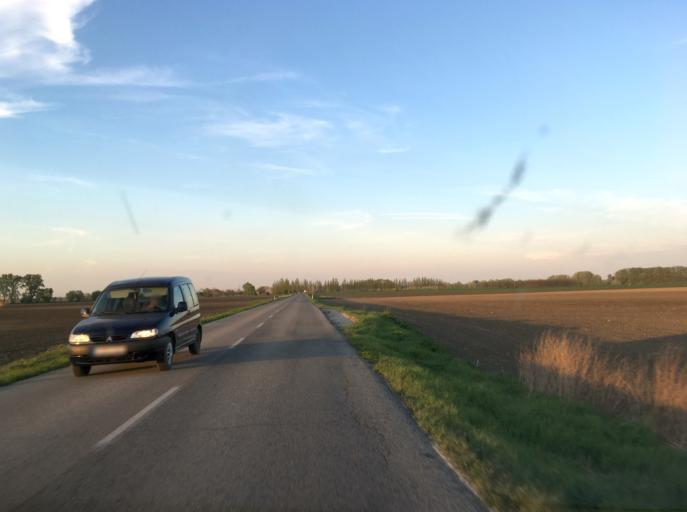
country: SK
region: Trnavsky
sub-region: Okres Dunajska Streda
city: Velky Meder
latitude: 47.9041
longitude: 17.8560
